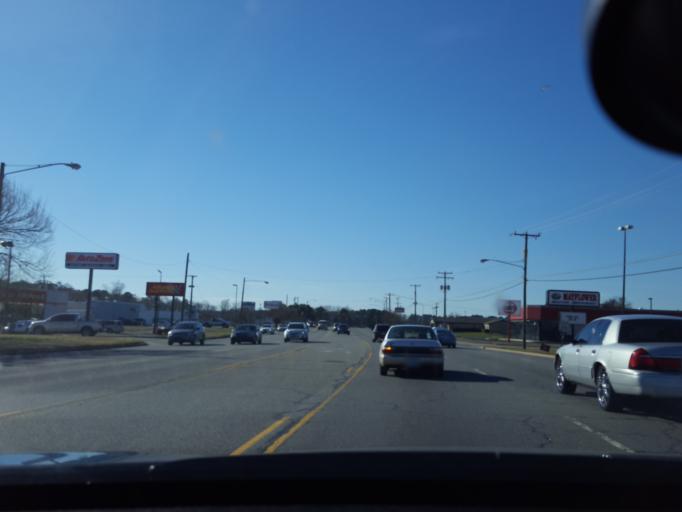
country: US
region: North Carolina
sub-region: Halifax County
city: Roanoke Rapids
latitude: 36.4345
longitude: -77.6385
